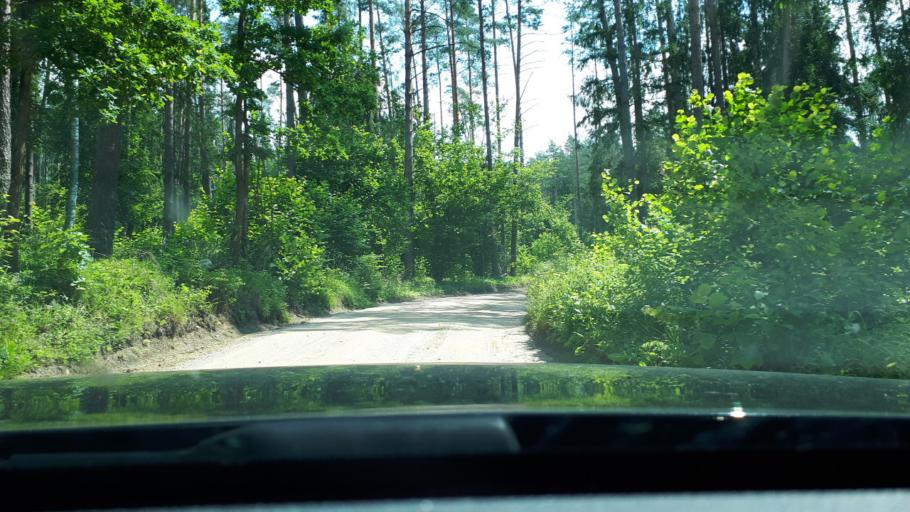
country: PL
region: Podlasie
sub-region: Powiat bialostocki
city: Suprasl
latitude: 53.2288
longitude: 23.3463
